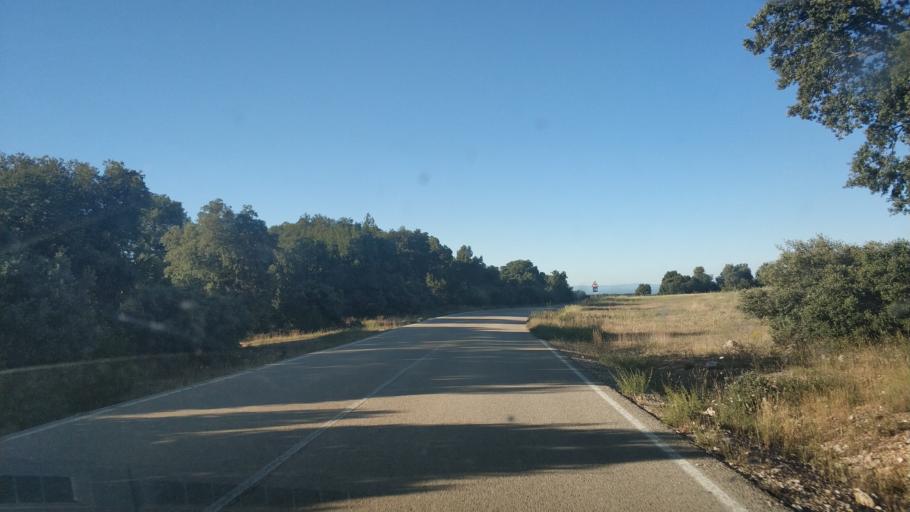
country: ES
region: Castille and Leon
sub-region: Provincia de Soria
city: Liceras
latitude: 41.4513
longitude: -3.2145
